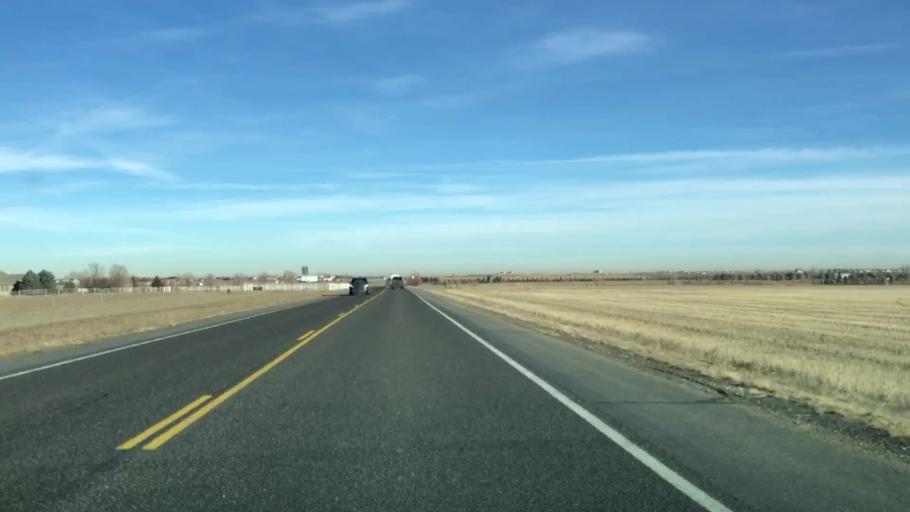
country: US
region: Colorado
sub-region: Weld County
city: Windsor
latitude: 40.4201
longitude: -104.9443
